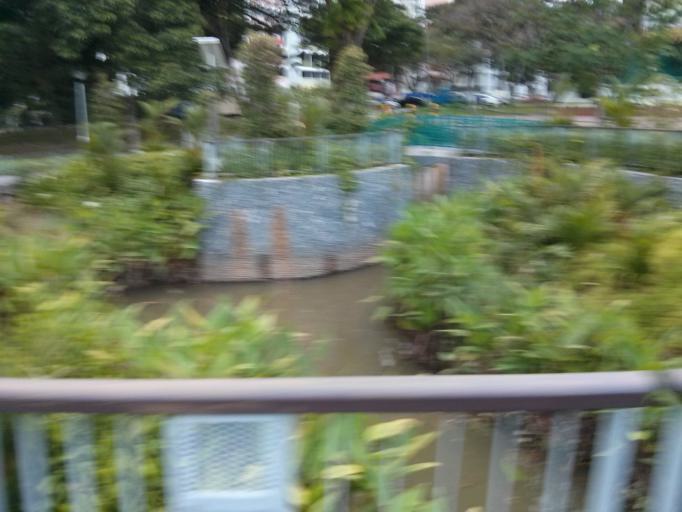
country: SG
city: Singapore
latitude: 1.3208
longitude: 103.7512
